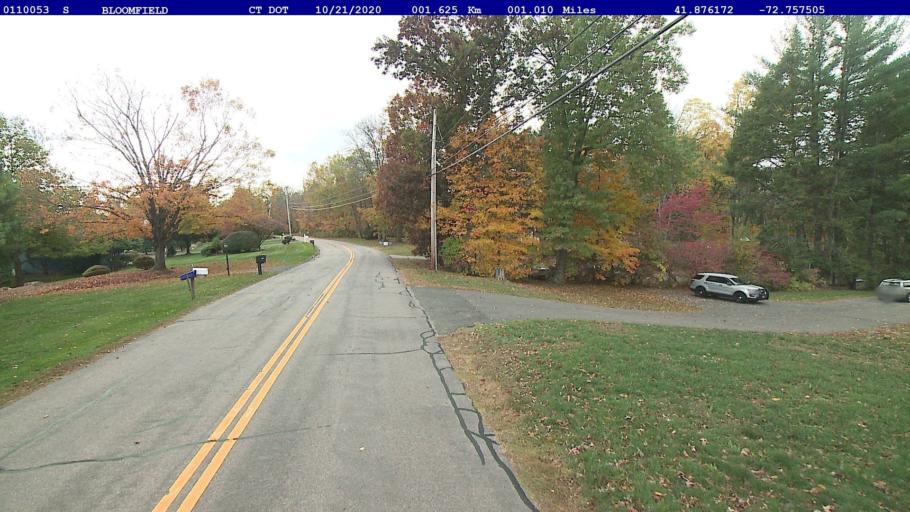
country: US
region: Connecticut
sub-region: Hartford County
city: Tariffville
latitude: 41.8762
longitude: -72.7575
